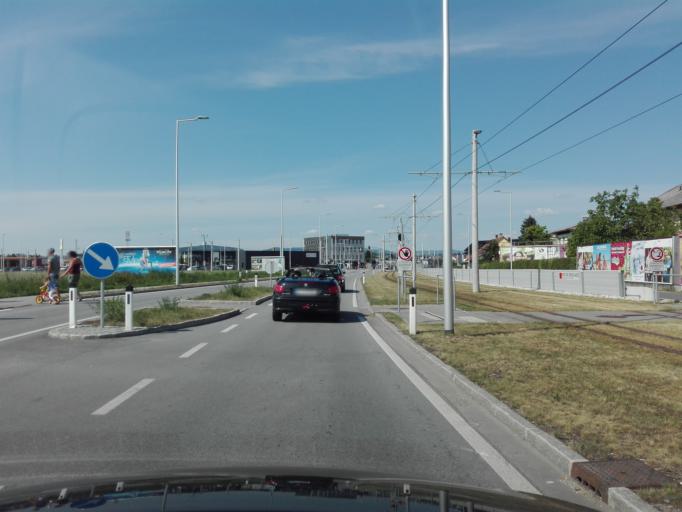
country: AT
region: Upper Austria
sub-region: Politischer Bezirk Linz-Land
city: Traun
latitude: 48.2320
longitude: 14.2344
